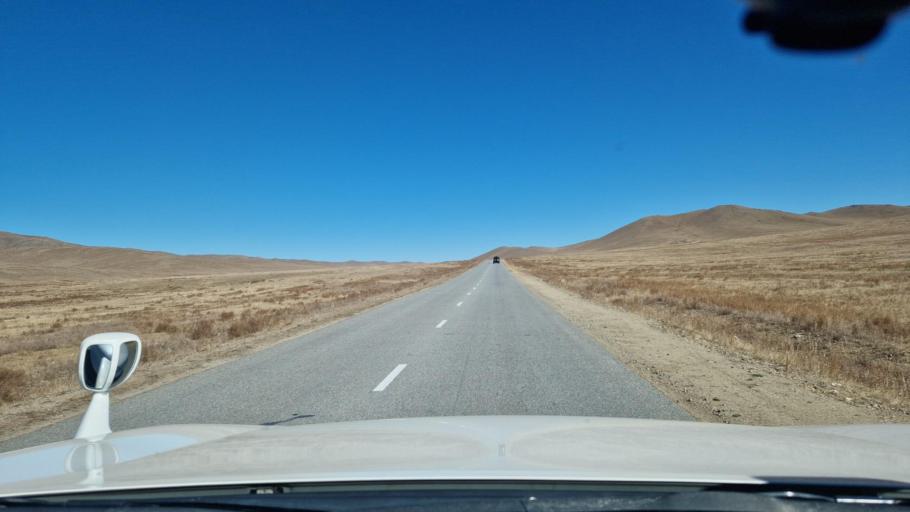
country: MN
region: Central Aimak
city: Bayandelger
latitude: 47.7059
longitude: 108.5630
